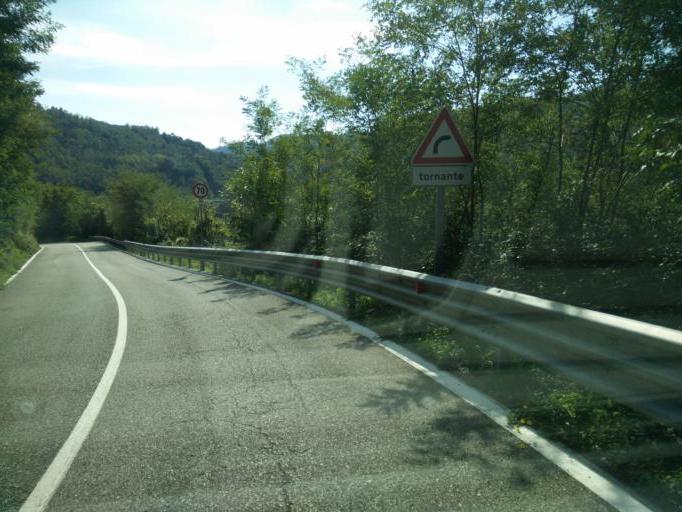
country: IT
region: Liguria
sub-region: Provincia di La Spezia
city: Carrodano
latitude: 44.2425
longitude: 9.6595
